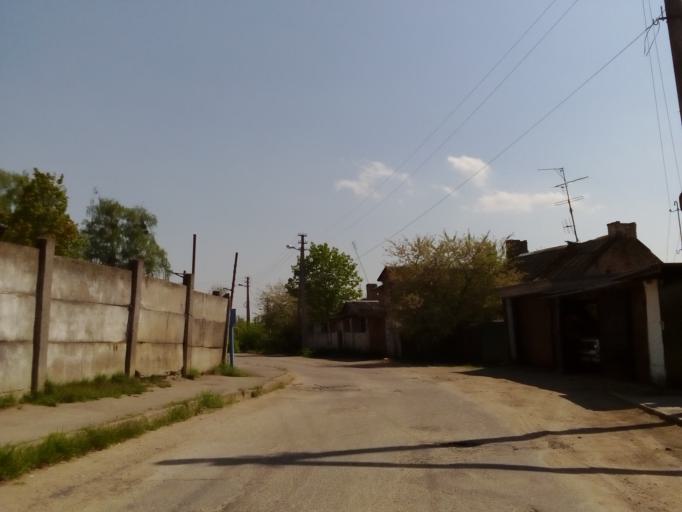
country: BY
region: Grodnenskaya
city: Hrodna
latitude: 53.6661
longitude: 23.8490
